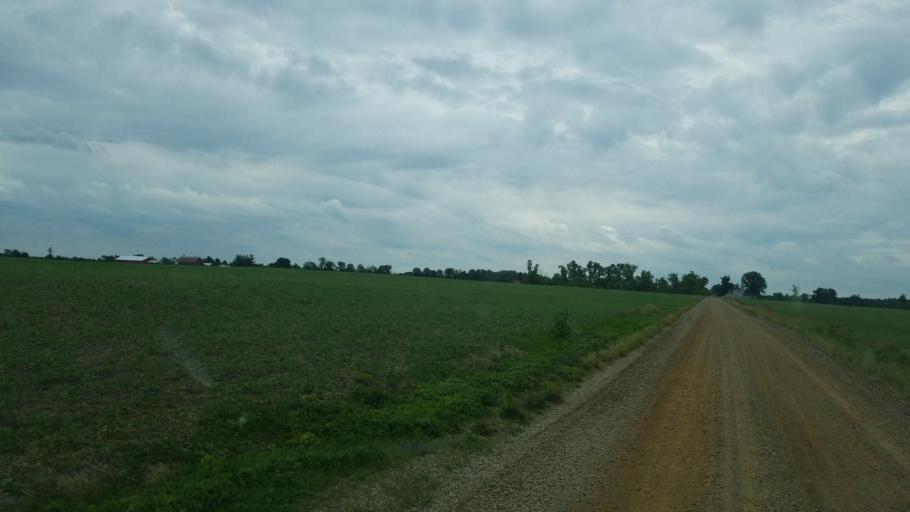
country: US
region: Michigan
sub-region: Barry County
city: Nashville
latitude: 42.6613
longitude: -84.9755
